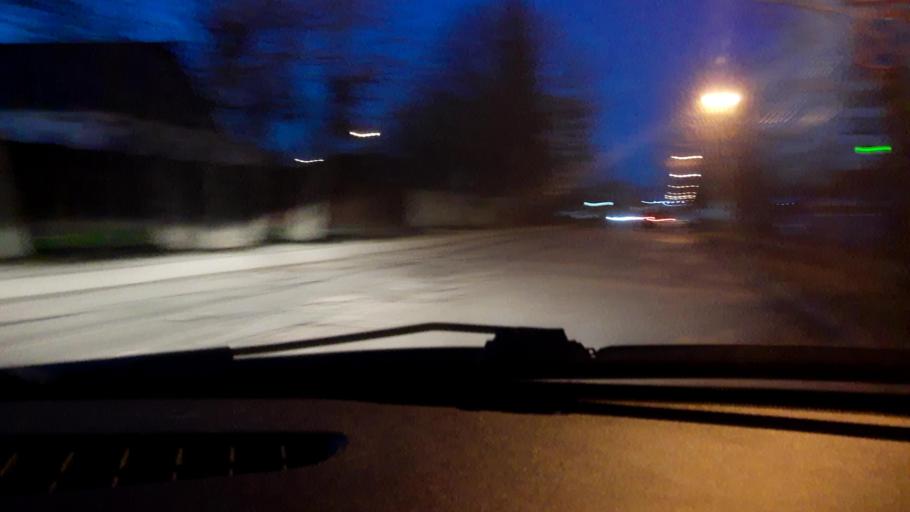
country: RU
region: Bashkortostan
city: Avdon
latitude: 54.6955
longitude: 55.8221
